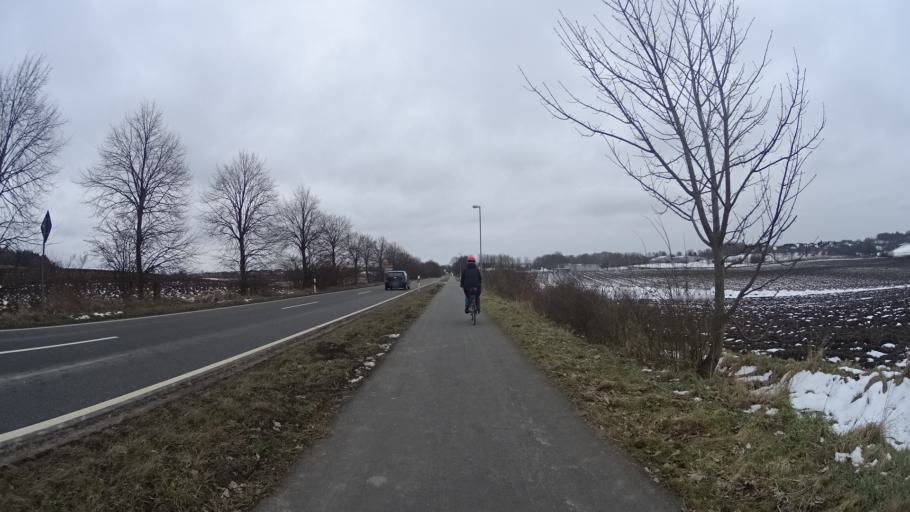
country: DE
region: Schleswig-Holstein
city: Lutjenburg
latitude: 54.3036
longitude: 10.5770
